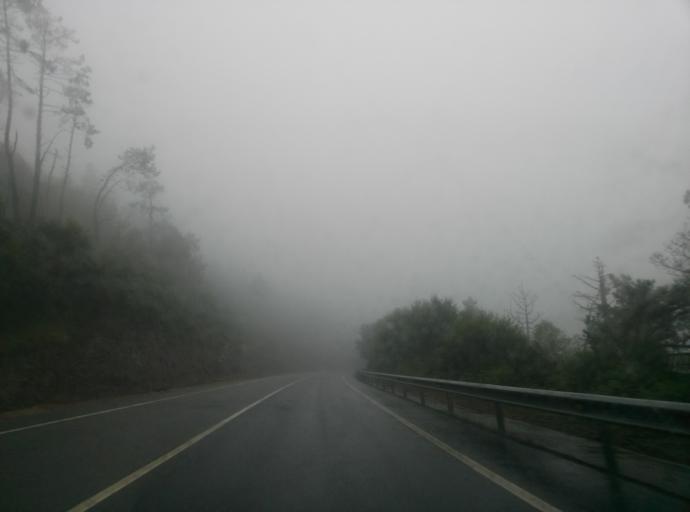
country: ES
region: Galicia
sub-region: Provincia de Lugo
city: Muras
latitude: 43.5189
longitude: -7.6717
